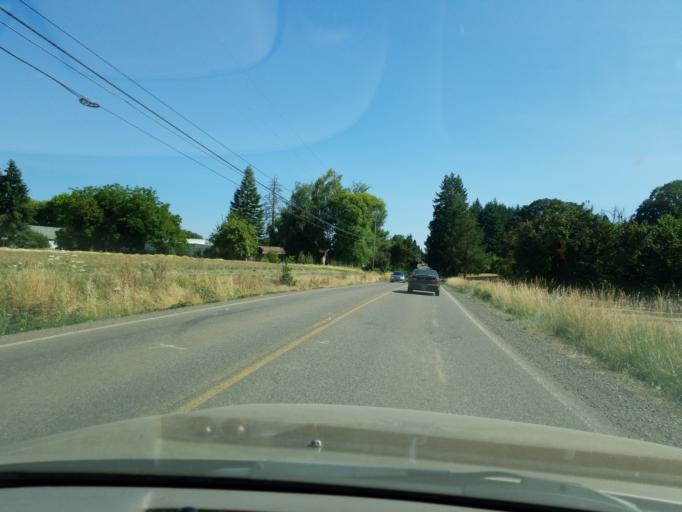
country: US
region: Oregon
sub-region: Yamhill County
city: McMinnville
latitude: 45.2497
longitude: -123.1993
